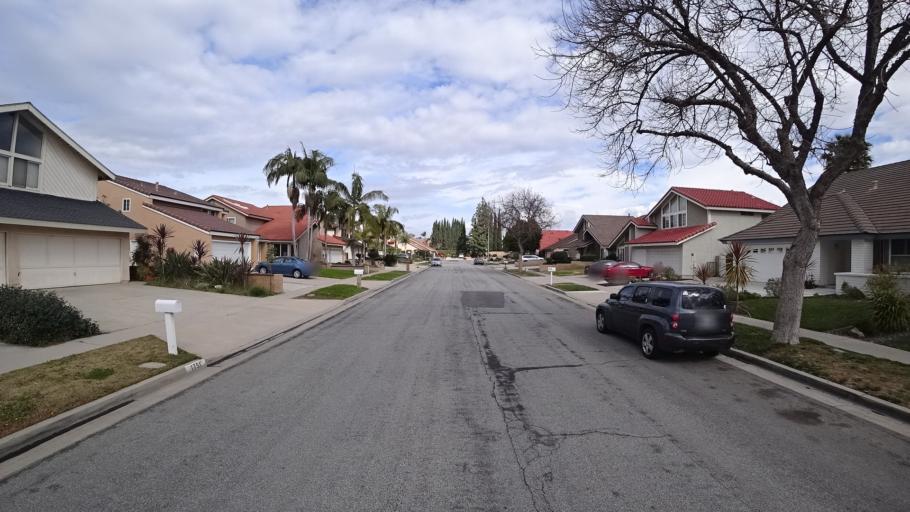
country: US
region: California
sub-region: Orange County
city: Placentia
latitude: 33.8662
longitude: -117.8643
